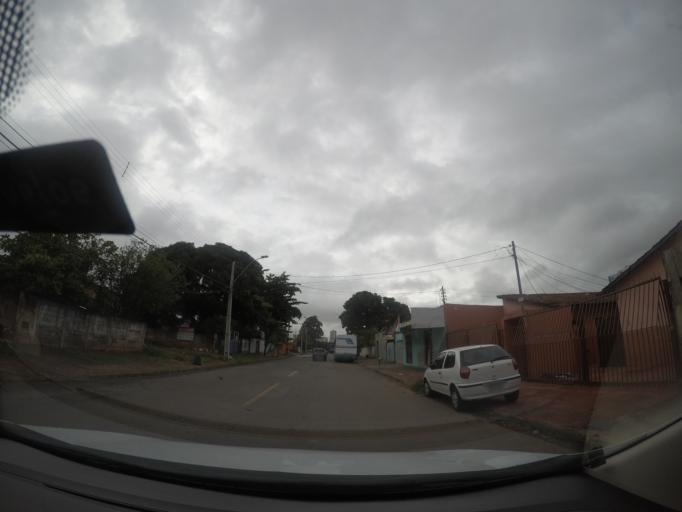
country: BR
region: Goias
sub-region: Goiania
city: Goiania
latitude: -16.7193
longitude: -49.2898
